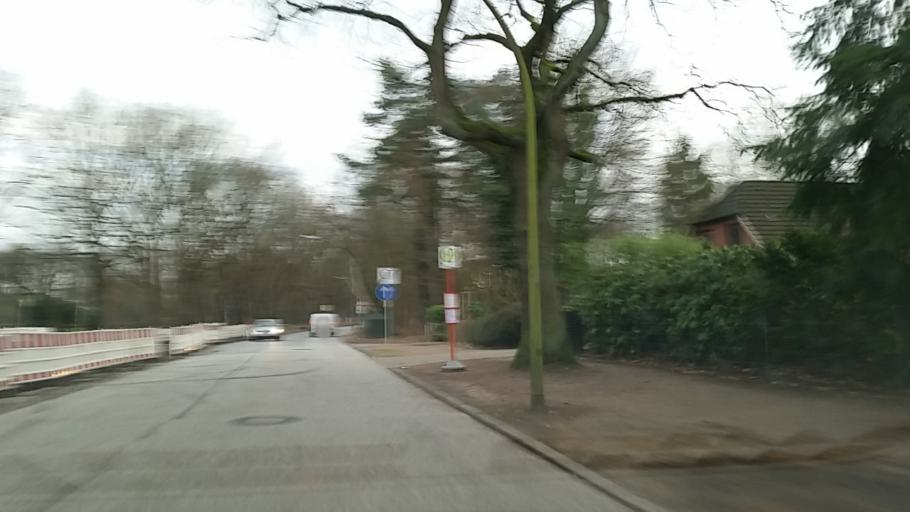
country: DE
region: Schleswig-Holstein
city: Wedel
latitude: 53.5718
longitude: 9.7421
